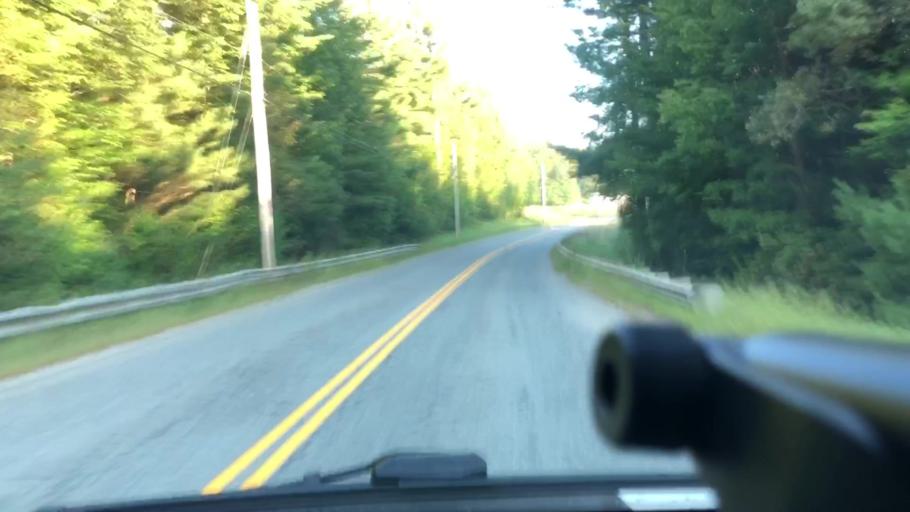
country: US
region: Massachusetts
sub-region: Franklin County
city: Ashfield
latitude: 42.5099
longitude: -72.8857
